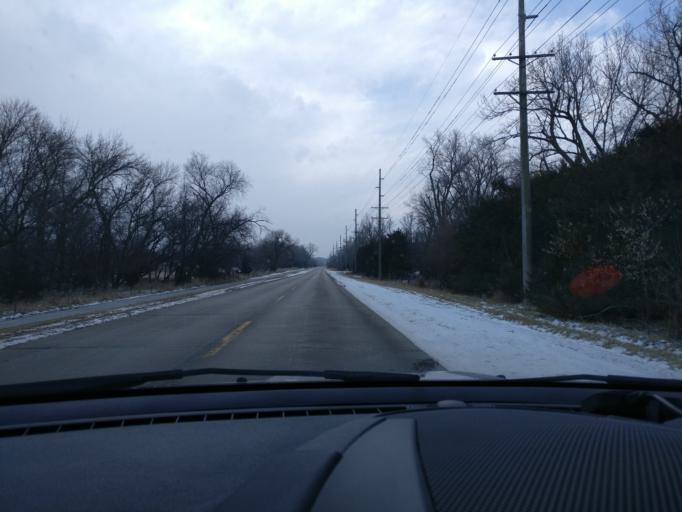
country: US
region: Nebraska
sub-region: Dodge County
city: Fremont
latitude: 41.4336
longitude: -96.5216
